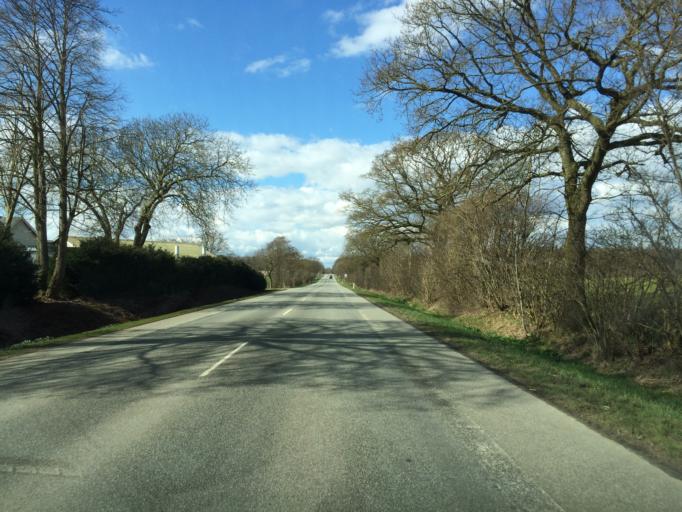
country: DK
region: South Denmark
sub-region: Middelfart Kommune
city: Brenderup
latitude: 55.4412
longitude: 9.9933
